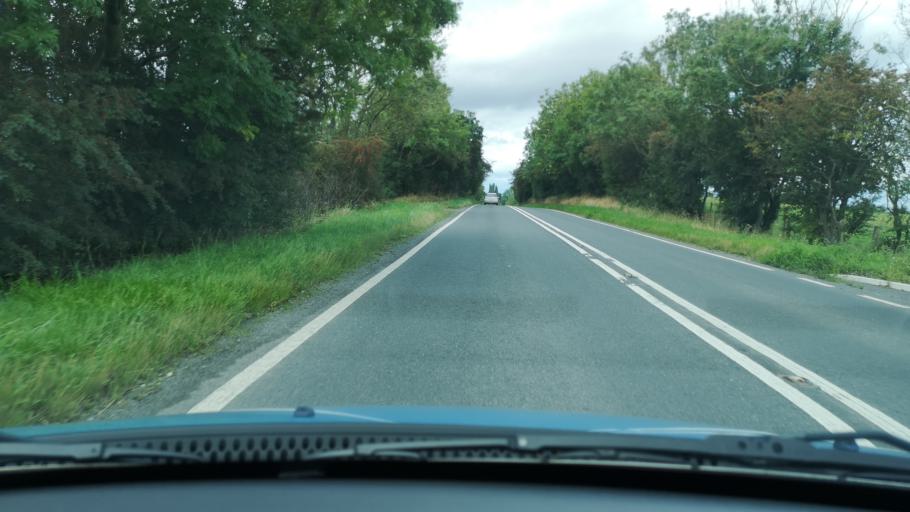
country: GB
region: England
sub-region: City and Borough of Wakefield
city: Low Ackworth
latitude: 53.6338
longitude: -1.3243
